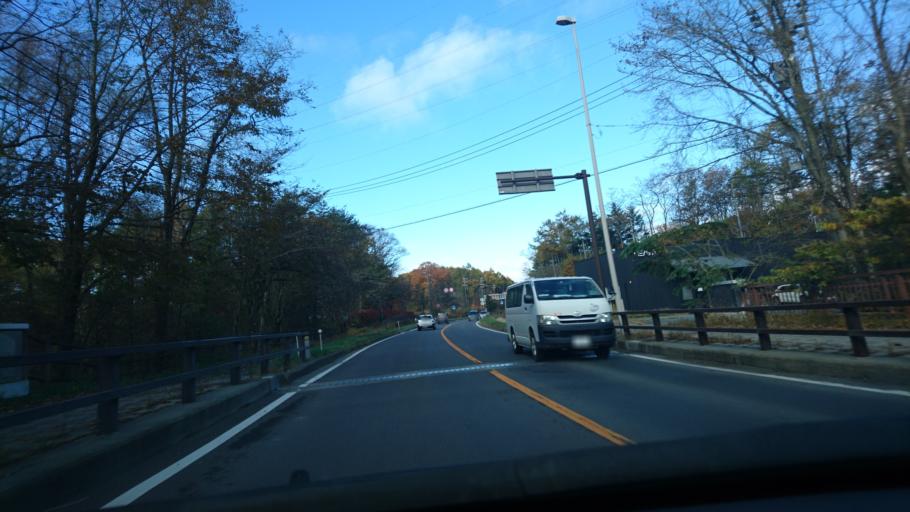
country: JP
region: Nagano
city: Saku
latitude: 36.3238
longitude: 138.6245
